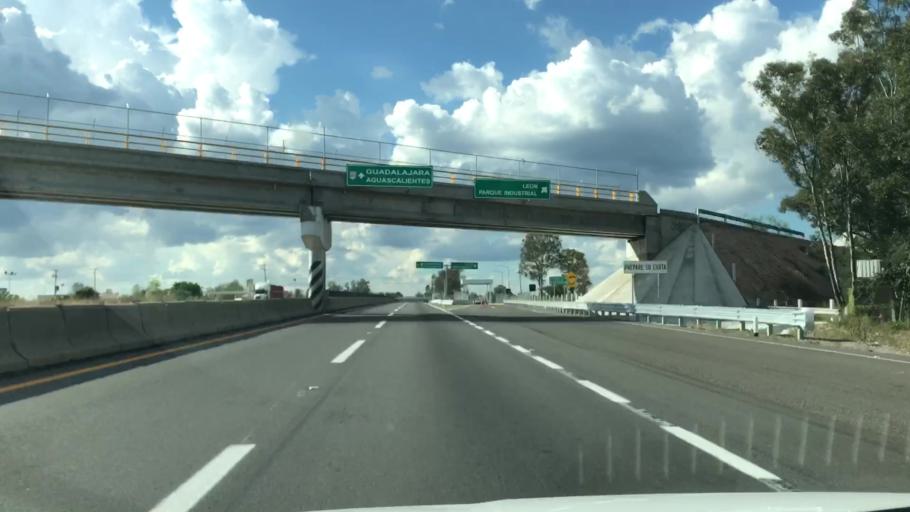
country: MX
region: Guanajuato
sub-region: Leon
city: Centro Familiar la Soledad
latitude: 21.0960
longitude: -101.7753
